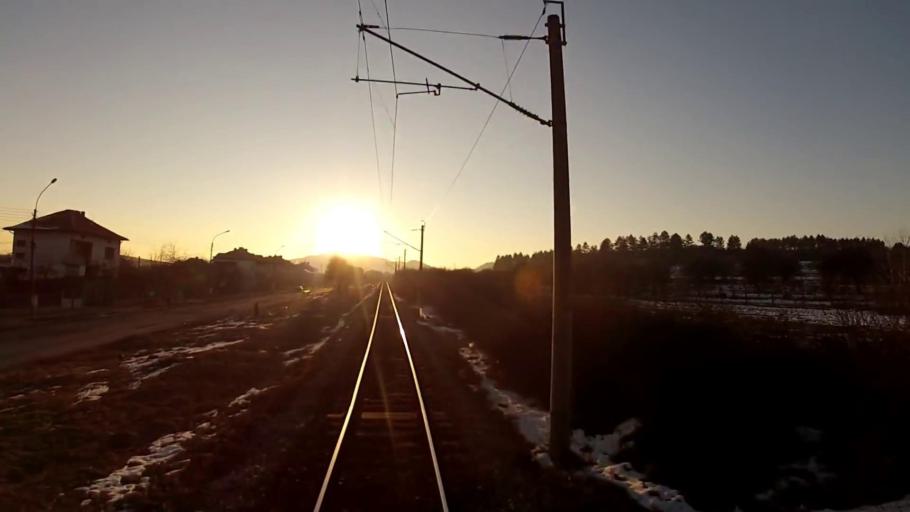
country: BG
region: Sofiya
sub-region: Obshtina Dragoman
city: Dragoman
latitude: 42.9136
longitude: 22.9384
